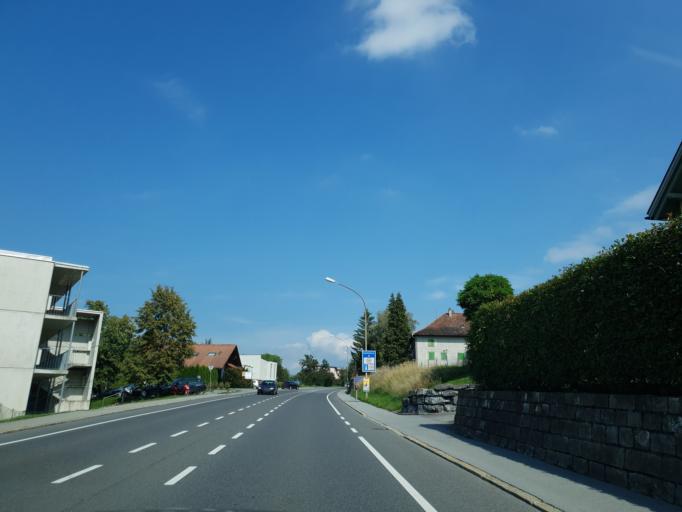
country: LI
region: Schellenberg
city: Schellenberg
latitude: 47.2202
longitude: 9.5736
